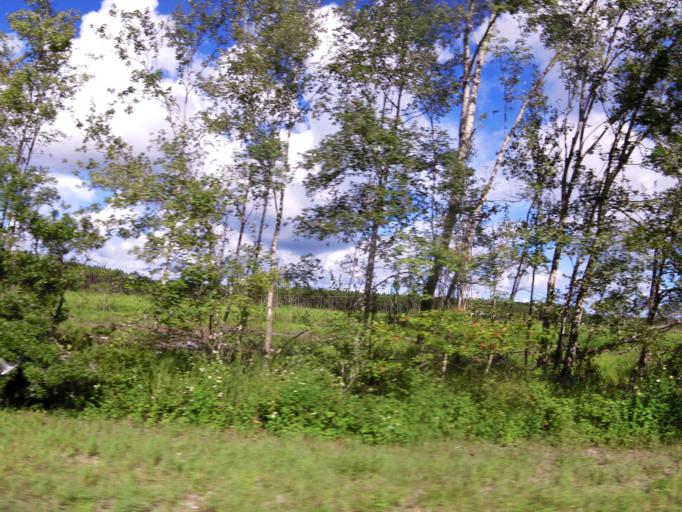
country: US
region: Georgia
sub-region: Camden County
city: Woodbine
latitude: 30.8827
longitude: -81.7067
